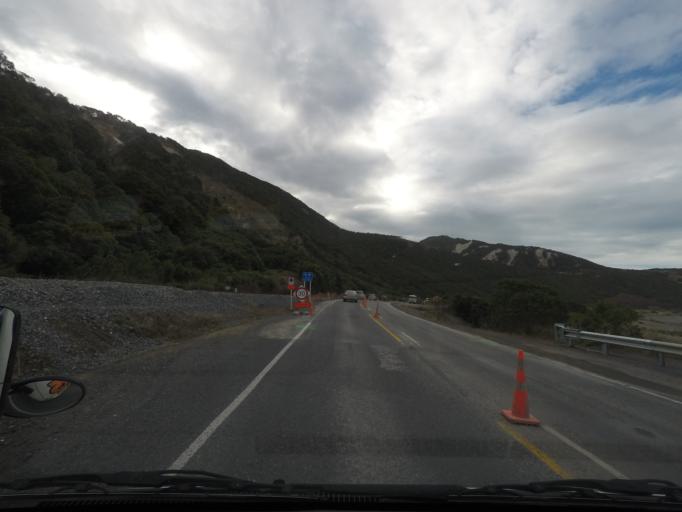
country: NZ
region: Canterbury
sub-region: Kaikoura District
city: Kaikoura
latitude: -42.2196
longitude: 173.8572
